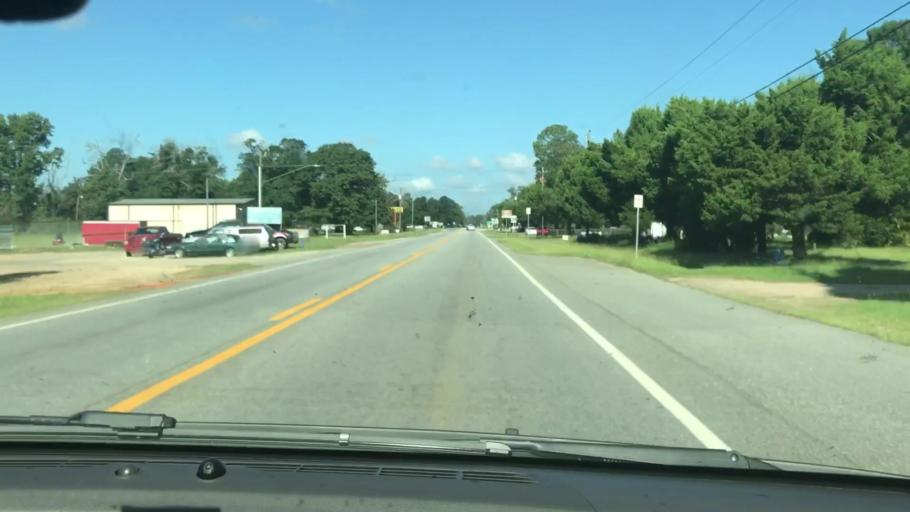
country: US
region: Georgia
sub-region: Quitman County
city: Georgetown
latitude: 31.8820
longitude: -85.0902
